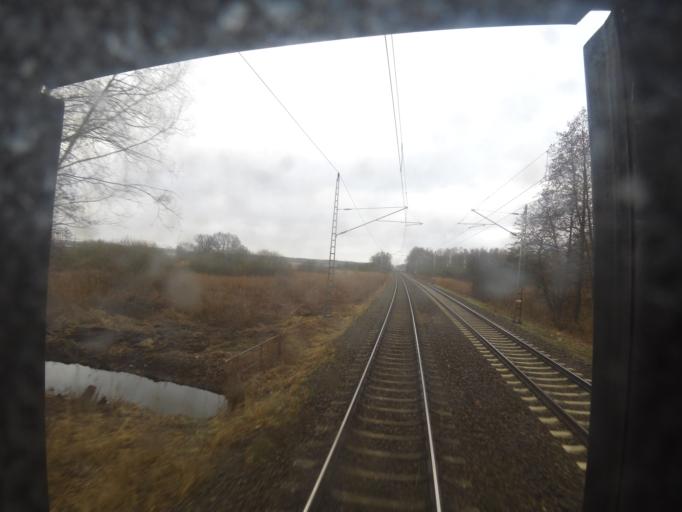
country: DE
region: Brandenburg
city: Zossen
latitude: 52.2074
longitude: 13.4406
